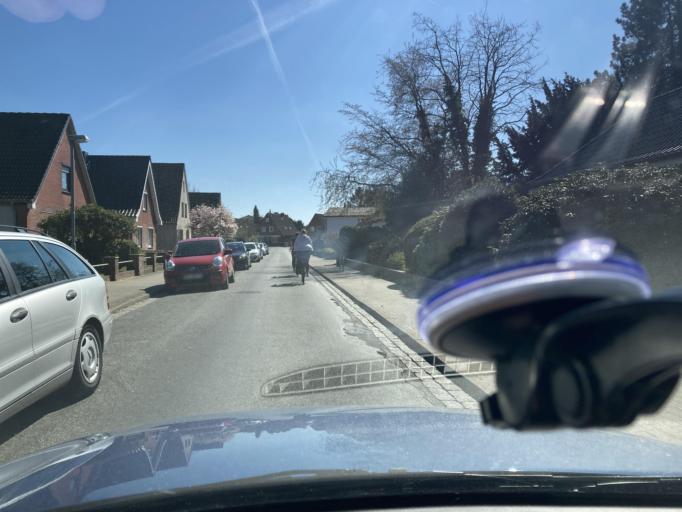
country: DE
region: Schleswig-Holstein
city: Wesseln
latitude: 54.1969
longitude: 9.0806
